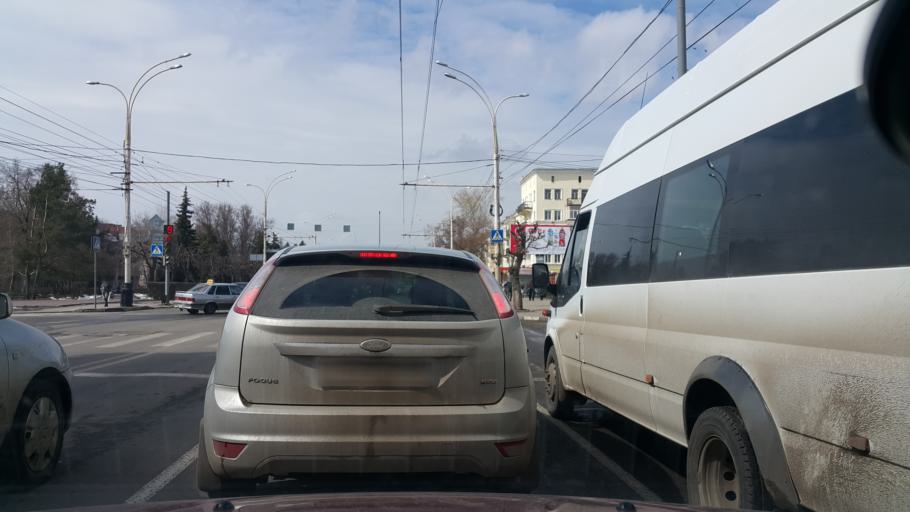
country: RU
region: Tambov
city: Tambov
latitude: 52.7062
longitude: 41.4700
